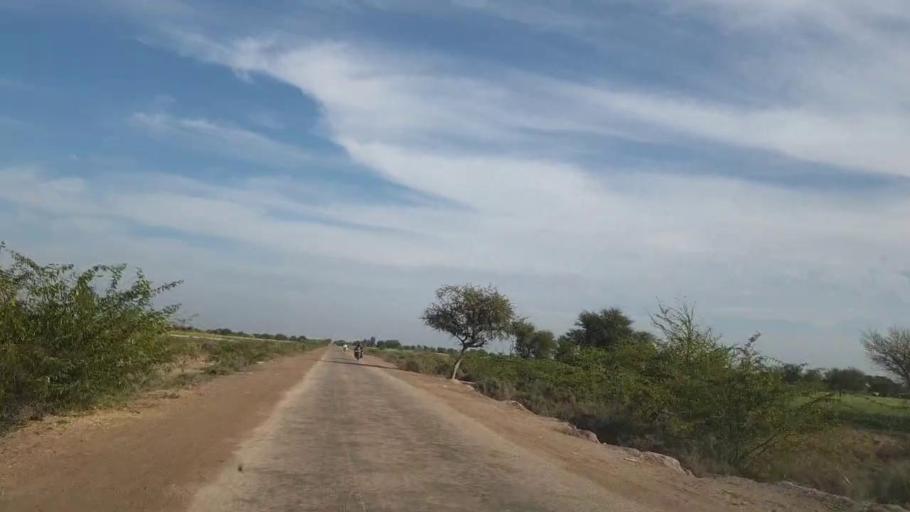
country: PK
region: Sindh
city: Pithoro
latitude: 25.6351
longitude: 69.3933
